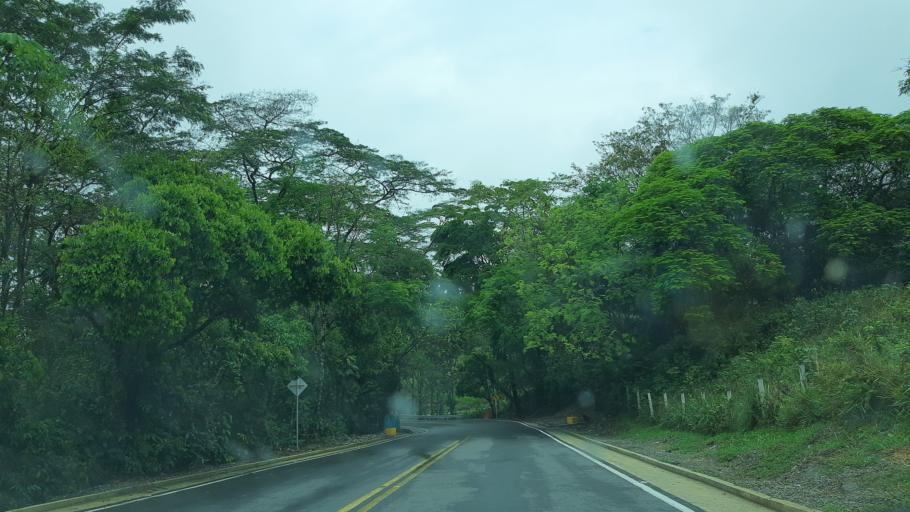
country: CO
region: Casanare
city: Sabanalarga
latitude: 4.7591
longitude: -73.0229
